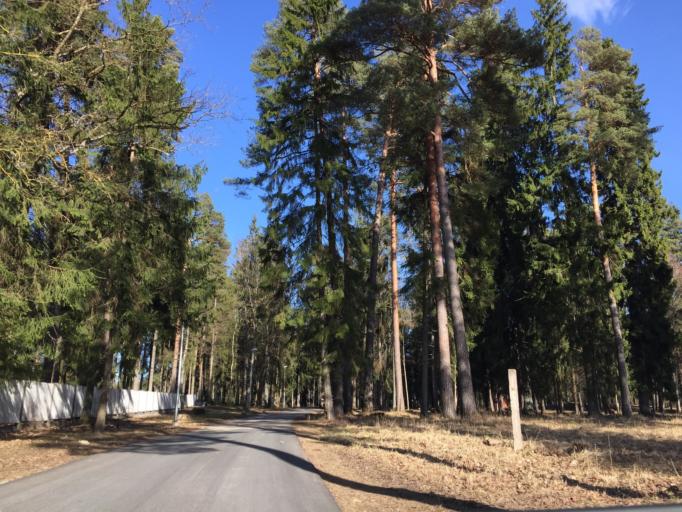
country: LV
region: Ogre
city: Ogre
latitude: 56.8165
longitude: 24.6204
